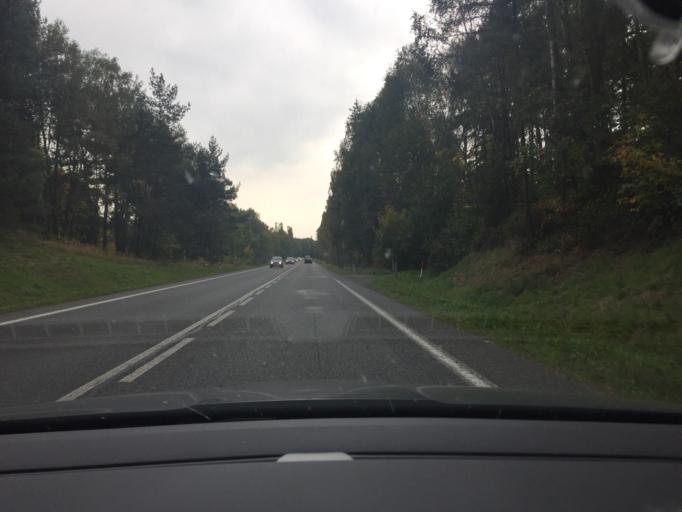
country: CZ
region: Central Bohemia
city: Milin
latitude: 49.6635
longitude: 14.0589
